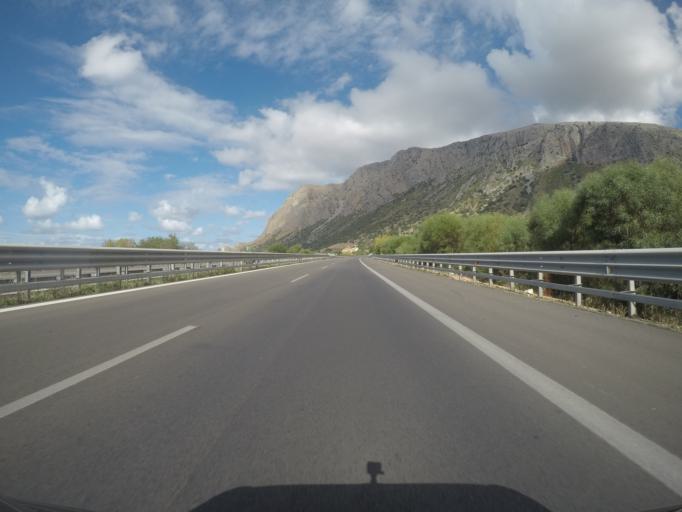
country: IT
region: Sicily
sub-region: Palermo
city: Cinisi
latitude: 38.1465
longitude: 13.1081
